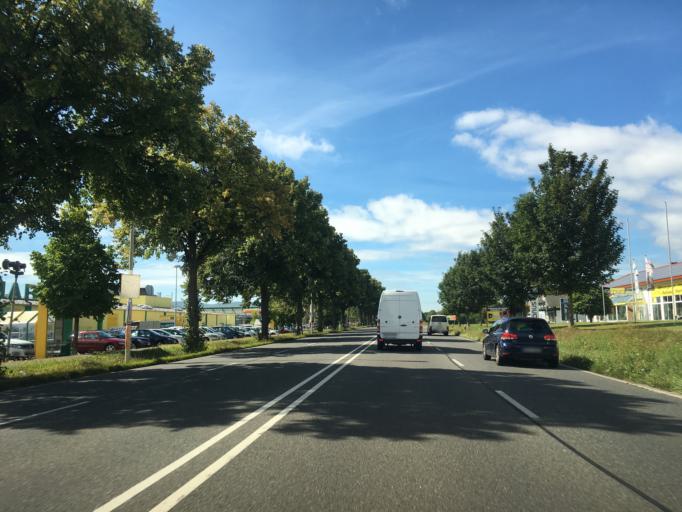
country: DE
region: Lower Saxony
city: Hameln
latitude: 52.0834
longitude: 9.3411
